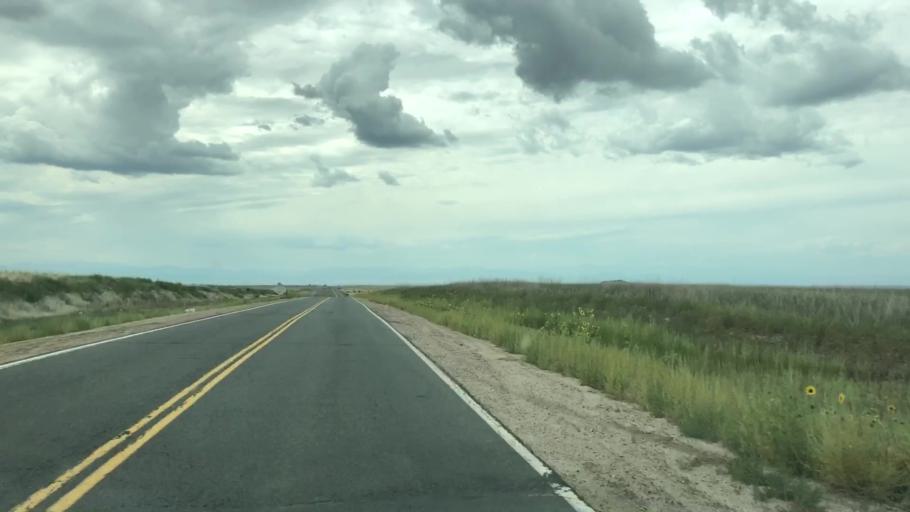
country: US
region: Colorado
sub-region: Adams County
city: Aurora
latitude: 39.7984
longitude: -104.6818
